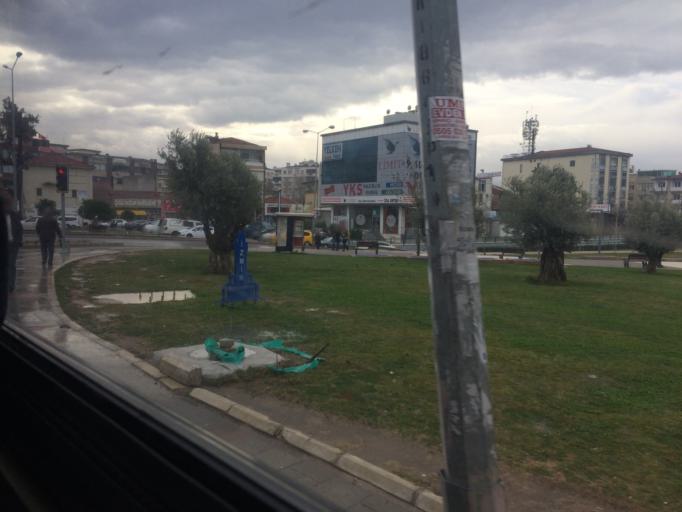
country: TR
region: Izmir
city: Karsiyaka
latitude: 38.4947
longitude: 27.0610
